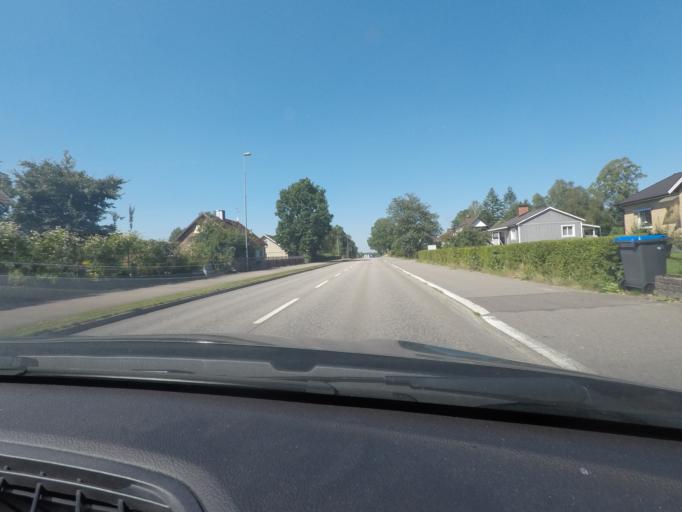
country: SE
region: Kronoberg
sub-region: Markaryds Kommun
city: Markaryd
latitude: 56.4510
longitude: 13.5967
